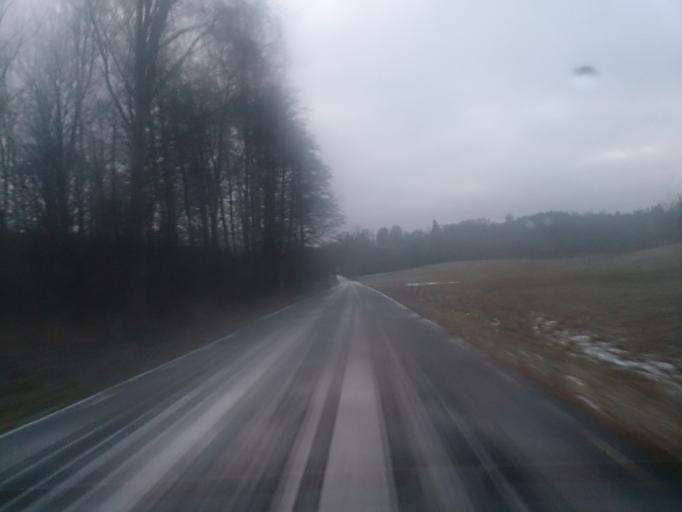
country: SE
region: OEstergoetland
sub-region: Atvidabergs Kommun
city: Atvidaberg
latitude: 58.2776
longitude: 16.1942
